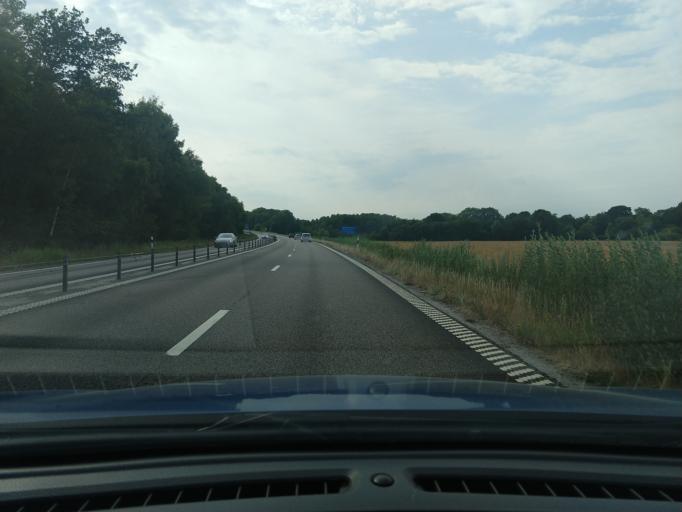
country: SE
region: Blekinge
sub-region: Karlskrona Kommun
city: Rodeby
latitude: 56.2016
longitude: 15.6726
